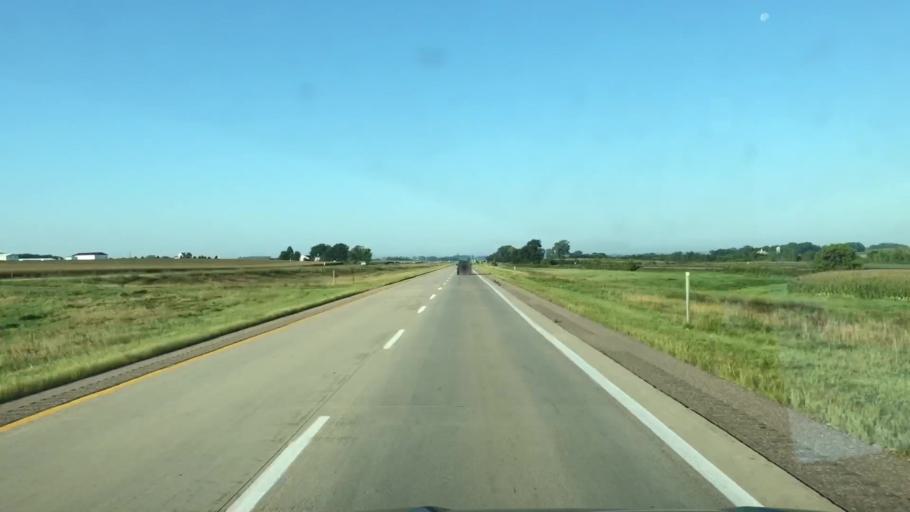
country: US
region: Iowa
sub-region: Sioux County
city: Alton
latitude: 43.0302
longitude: -95.9338
